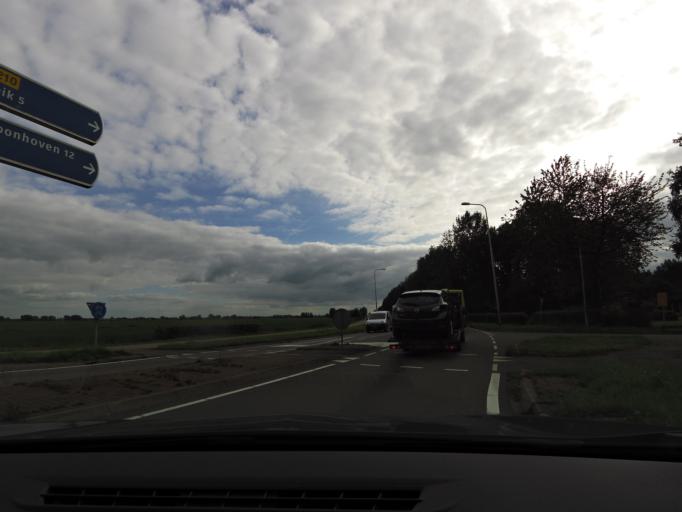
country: NL
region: Utrecht
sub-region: Gemeente Lopik
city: Lopik
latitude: 51.9943
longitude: 4.9684
